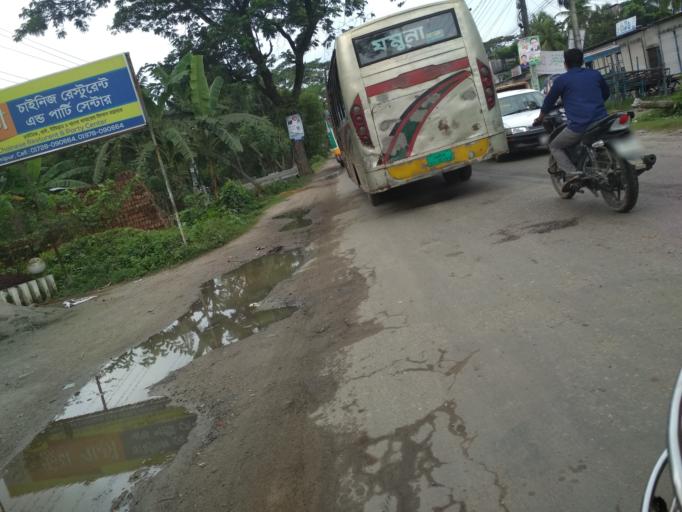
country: BD
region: Chittagong
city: Lakshmipur
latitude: 22.9454
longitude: 90.8226
